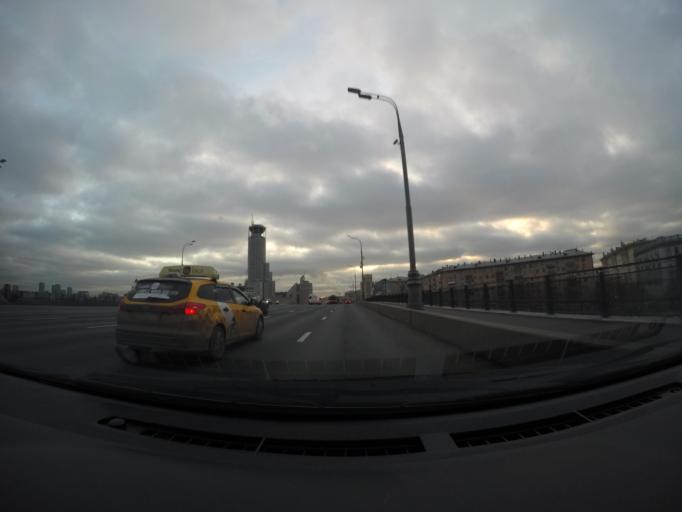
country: RU
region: Moscow
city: Zamoskvorech'ye
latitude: 55.7374
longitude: 37.6479
